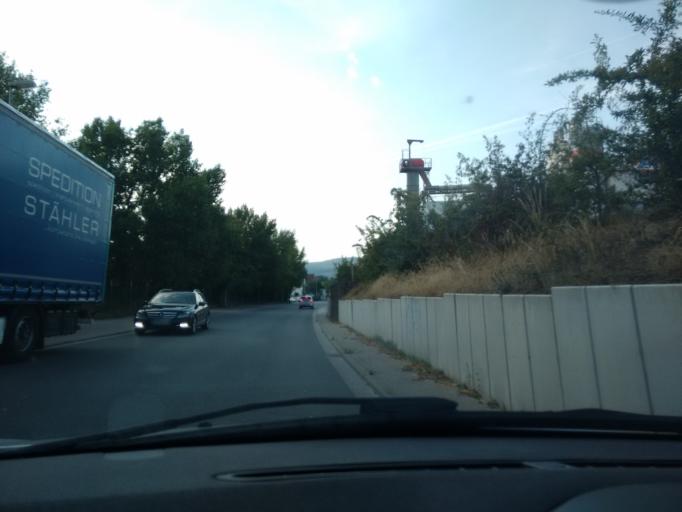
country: DE
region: Rheinland-Pfalz
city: Ingelheim am Rhein
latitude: 49.9879
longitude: 8.0358
